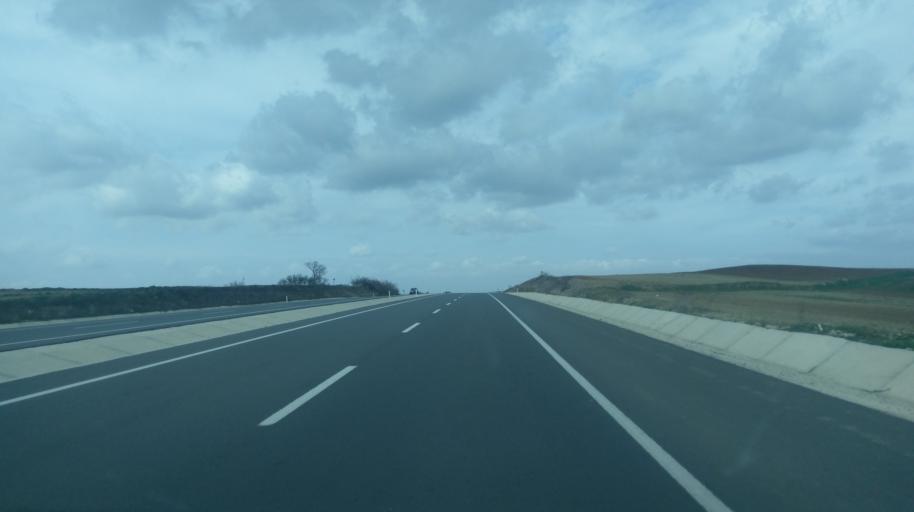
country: TR
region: Edirne
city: Ibriktepe
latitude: 41.0169
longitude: 26.6359
